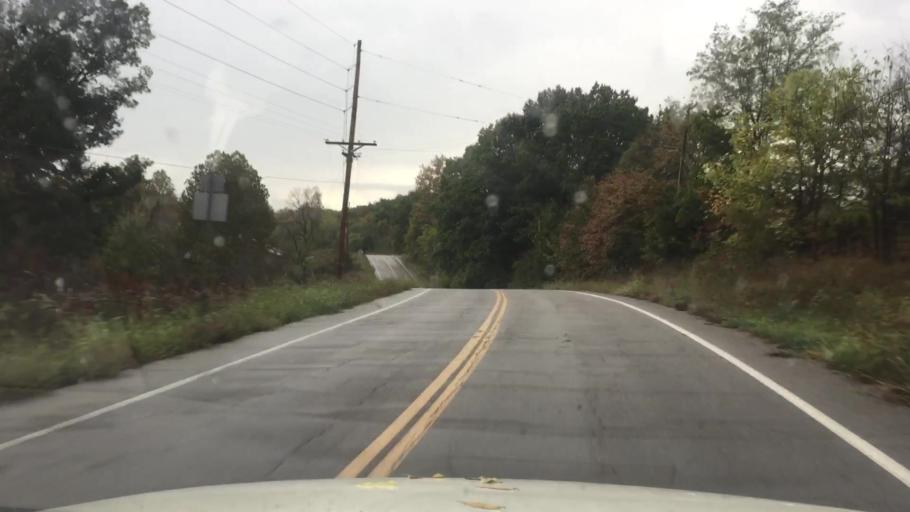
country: US
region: Missouri
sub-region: Boone County
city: Columbia
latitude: 38.8832
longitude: -92.4246
